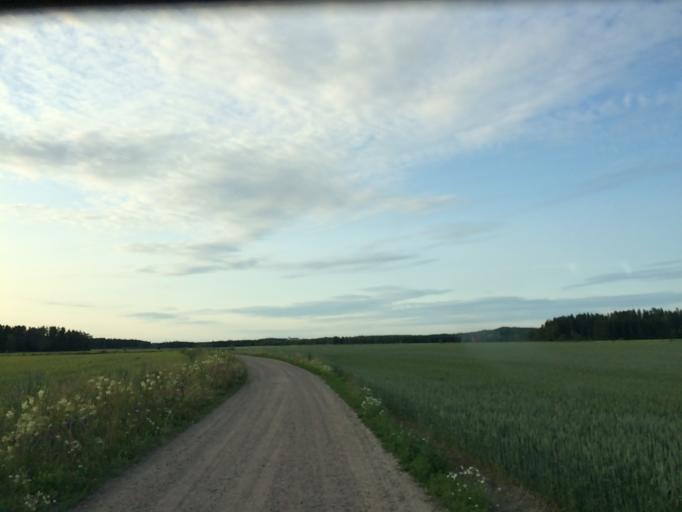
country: FI
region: Haeme
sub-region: Haemeenlinna
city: Janakkala
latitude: 60.8795
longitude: 24.6298
